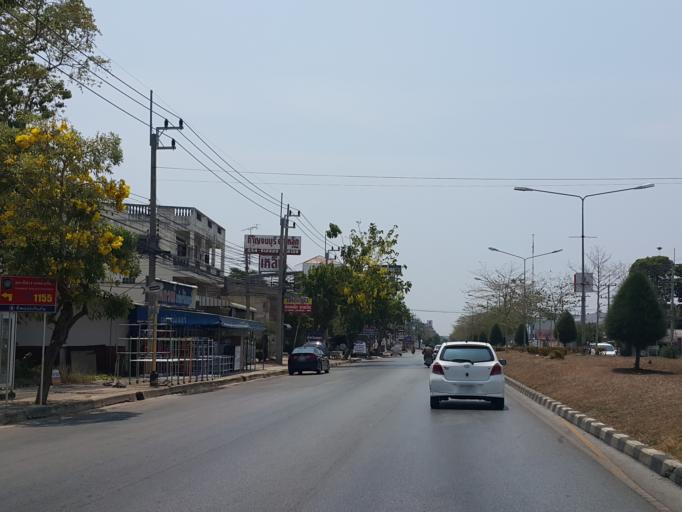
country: TH
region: Kanchanaburi
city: Kanchanaburi
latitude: 14.0431
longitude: 99.5133
